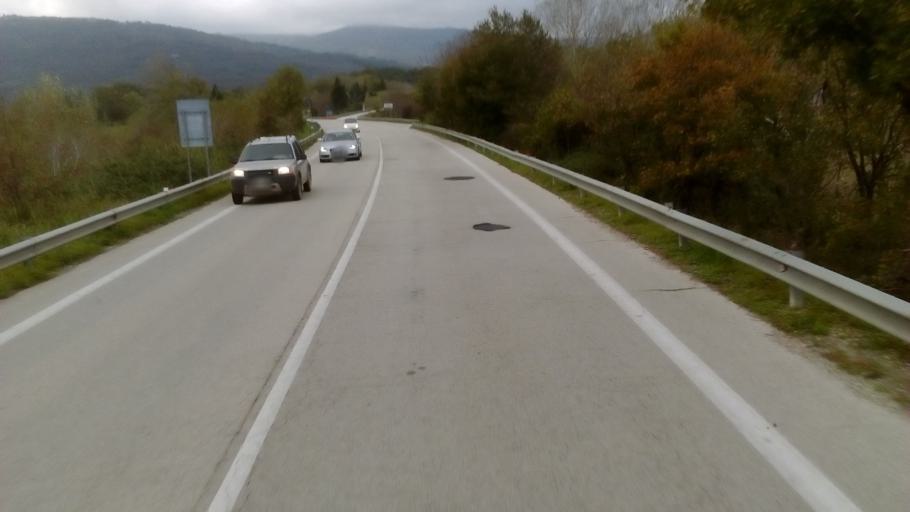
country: IT
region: Abruzzo
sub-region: Provincia di Chieti
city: Tufillo
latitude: 41.8966
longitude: 14.6235
